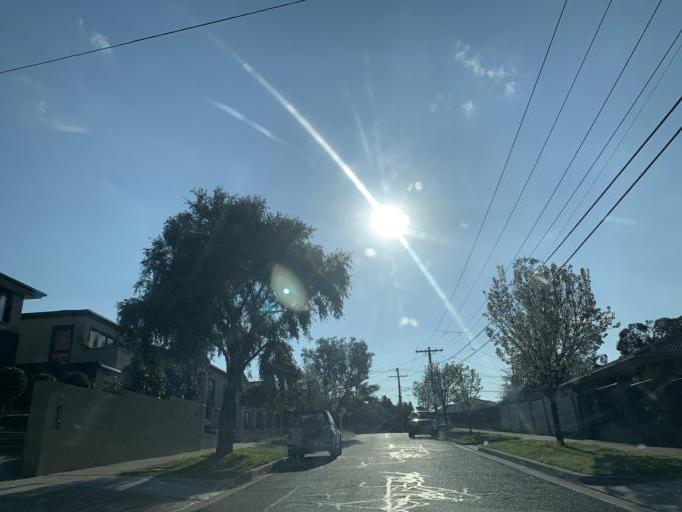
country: AU
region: Victoria
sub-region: Kingston
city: Mordialloc
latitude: -37.9970
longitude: 145.0887
